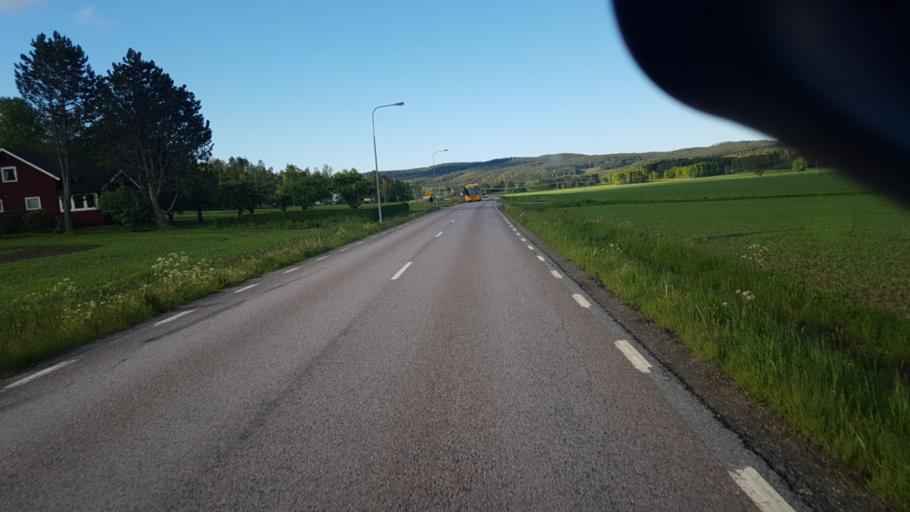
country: SE
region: Vaermland
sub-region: Arvika Kommun
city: Arvika
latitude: 59.5700
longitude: 12.5581
